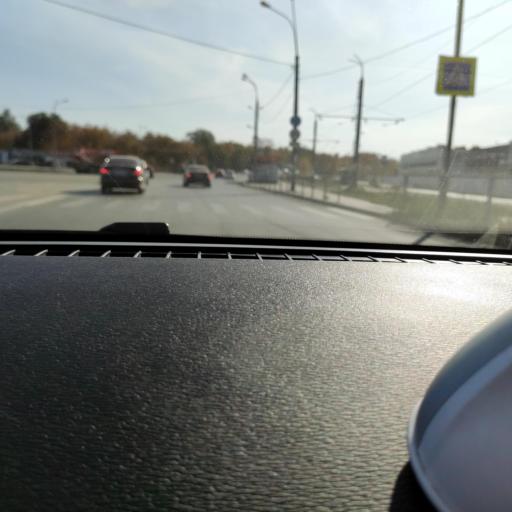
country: RU
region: Samara
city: Petra-Dubrava
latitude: 53.2262
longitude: 50.2819
